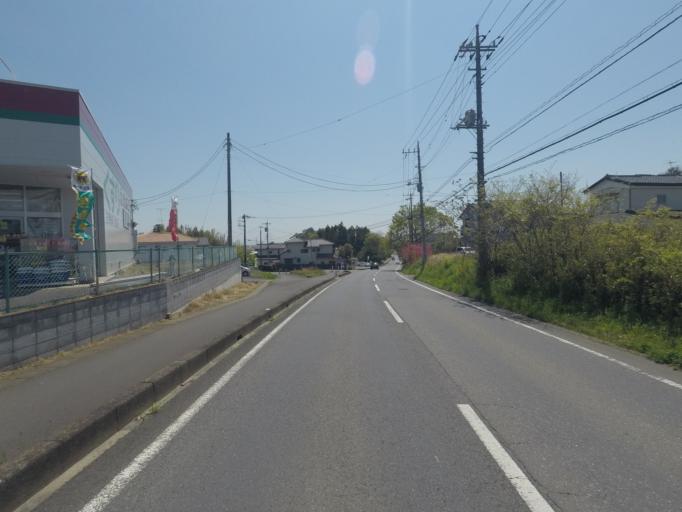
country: JP
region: Ibaraki
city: Ushiku
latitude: 35.9591
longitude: 140.1035
